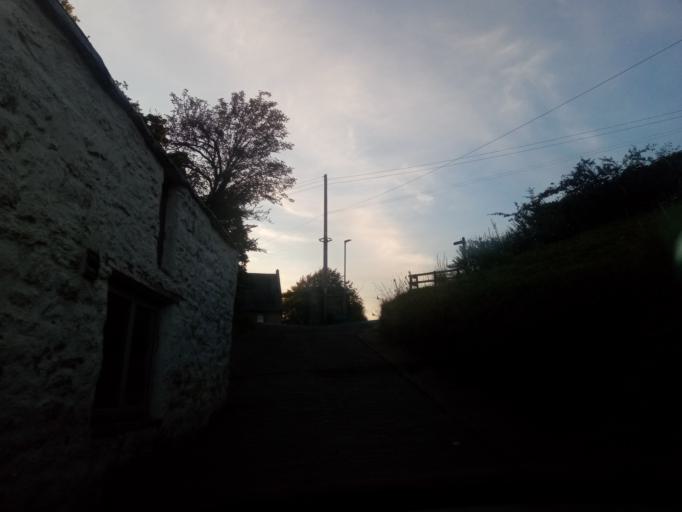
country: GB
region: England
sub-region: Northumberland
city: Bardon Mill
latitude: 54.7885
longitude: -2.3410
